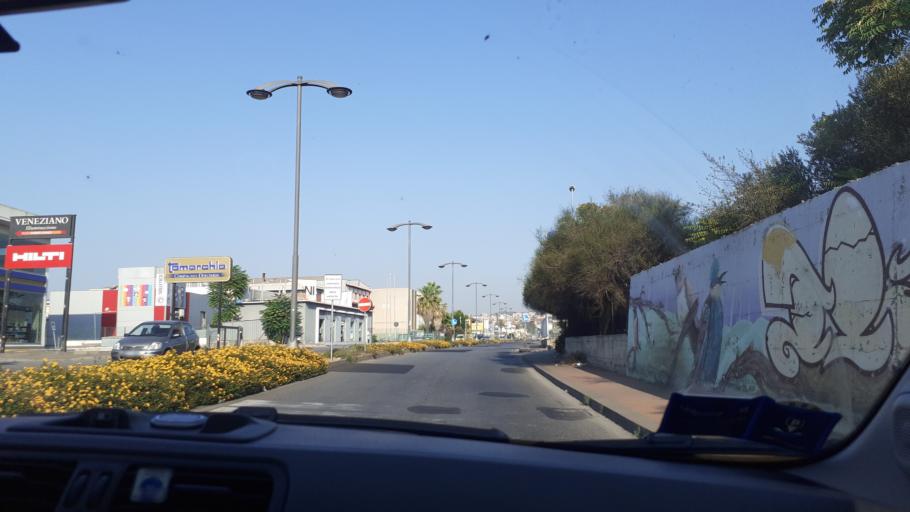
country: IT
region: Sicily
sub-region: Catania
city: Misterbianco
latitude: 37.5117
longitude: 15.0329
